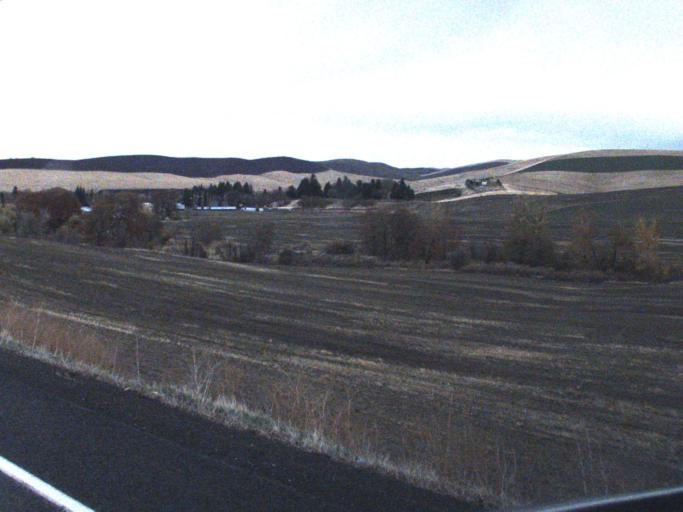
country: US
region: Washington
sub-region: Walla Walla County
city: Waitsburg
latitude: 46.2532
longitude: -118.1489
